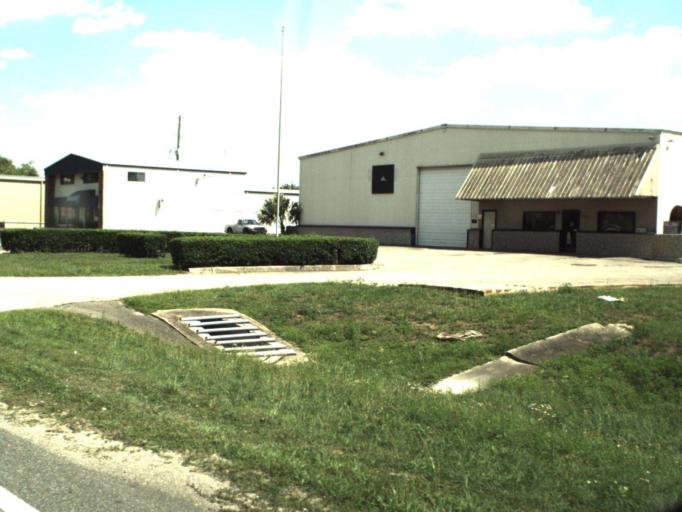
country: US
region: Florida
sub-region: Marion County
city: Ocala
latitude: 29.1715
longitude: -82.1538
